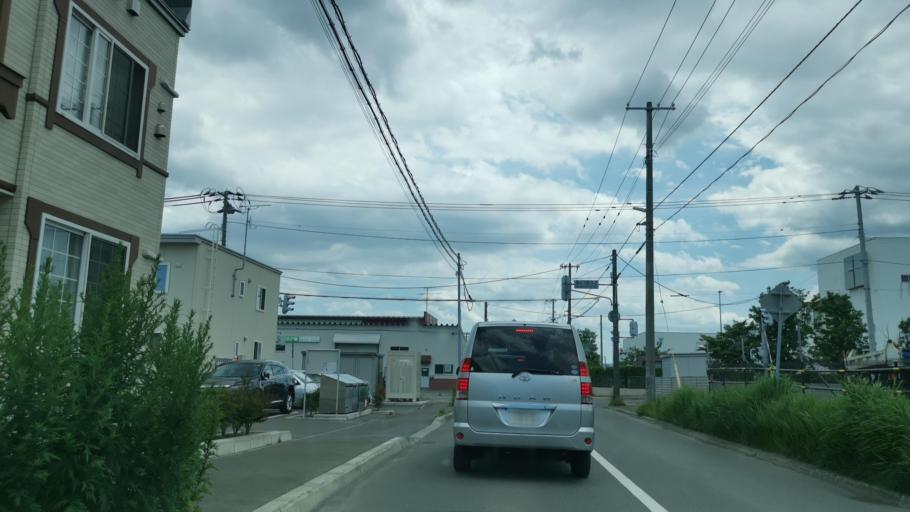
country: JP
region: Hokkaido
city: Sapporo
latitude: 43.0714
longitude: 141.4167
